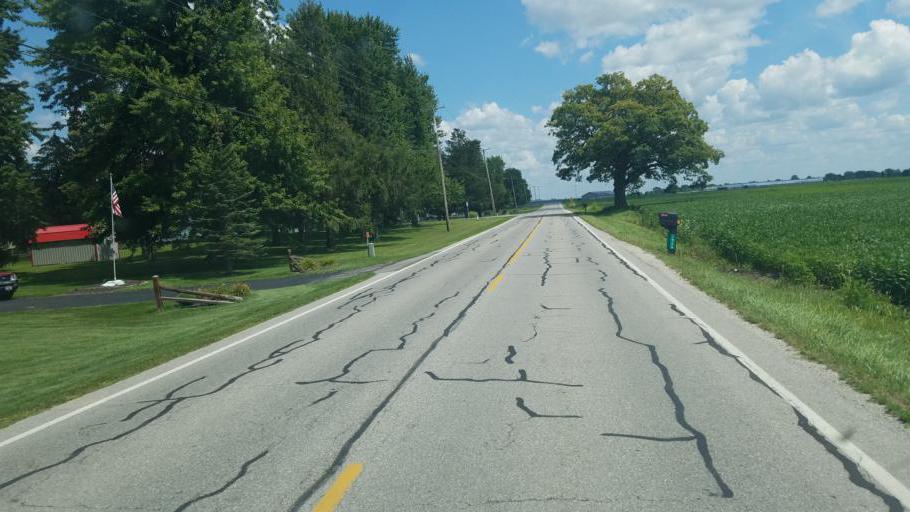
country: US
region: Ohio
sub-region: Marion County
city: Marion
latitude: 40.6150
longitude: -83.0788
